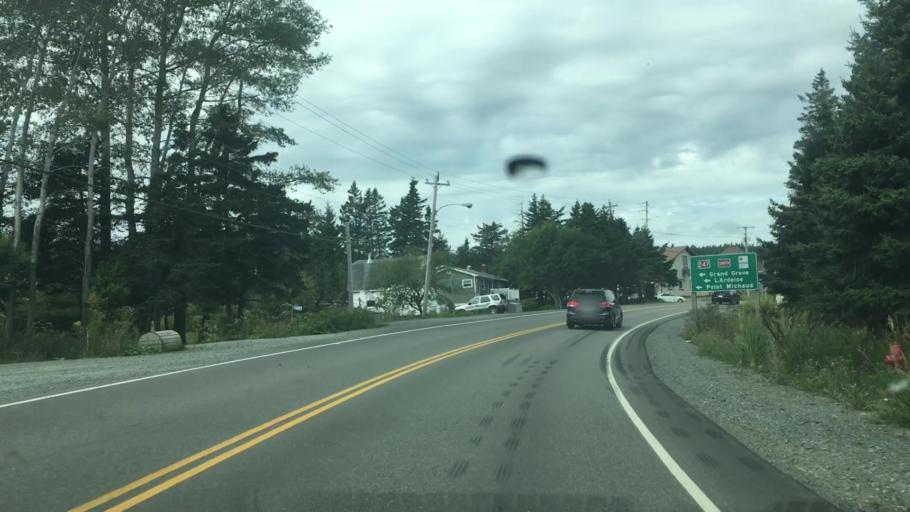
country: CA
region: Nova Scotia
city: Princeville
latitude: 45.6515
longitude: -60.8561
